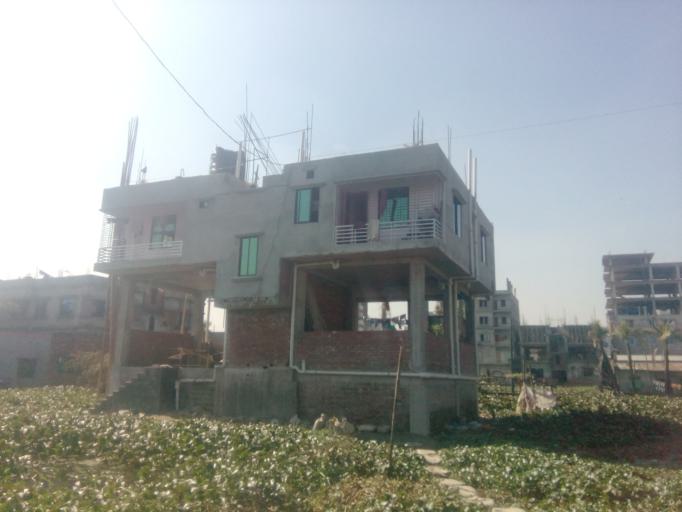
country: BD
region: Dhaka
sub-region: Dhaka
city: Dhaka
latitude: 23.7058
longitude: 90.4750
